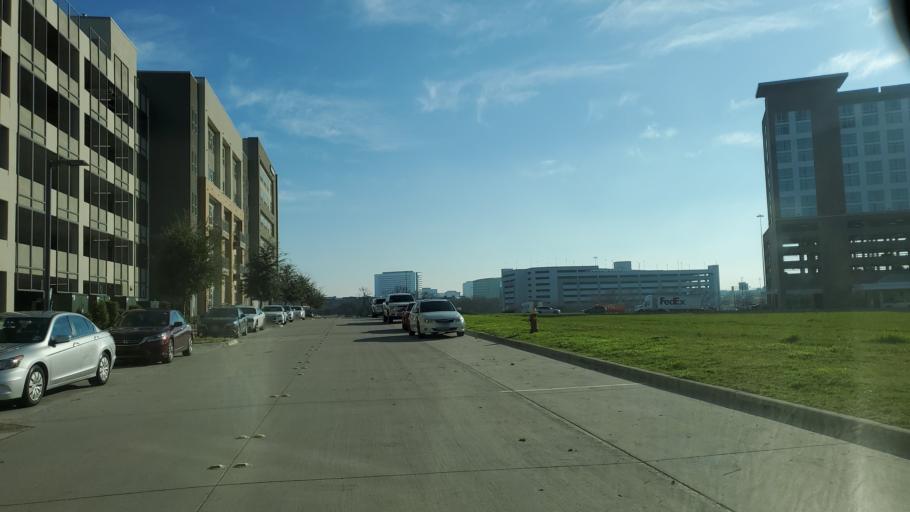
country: US
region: Texas
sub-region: Collin County
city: Plano
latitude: 33.0024
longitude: -96.7059
